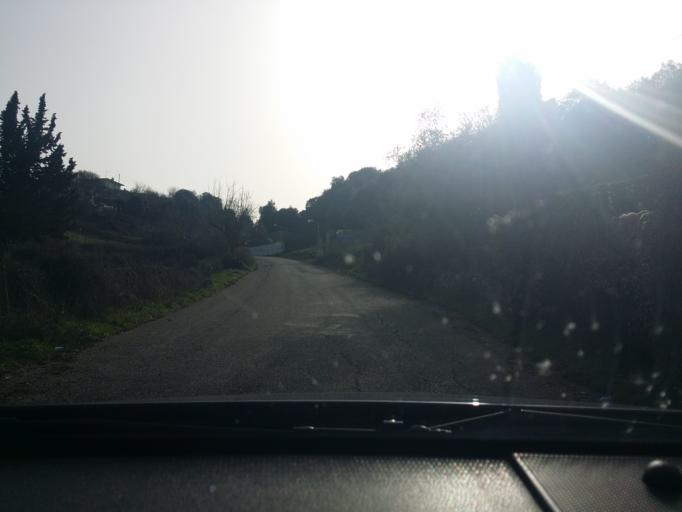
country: GR
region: West Greece
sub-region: Nomos Aitolias kai Akarnanias
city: Katouna
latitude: 38.8291
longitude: 21.0746
